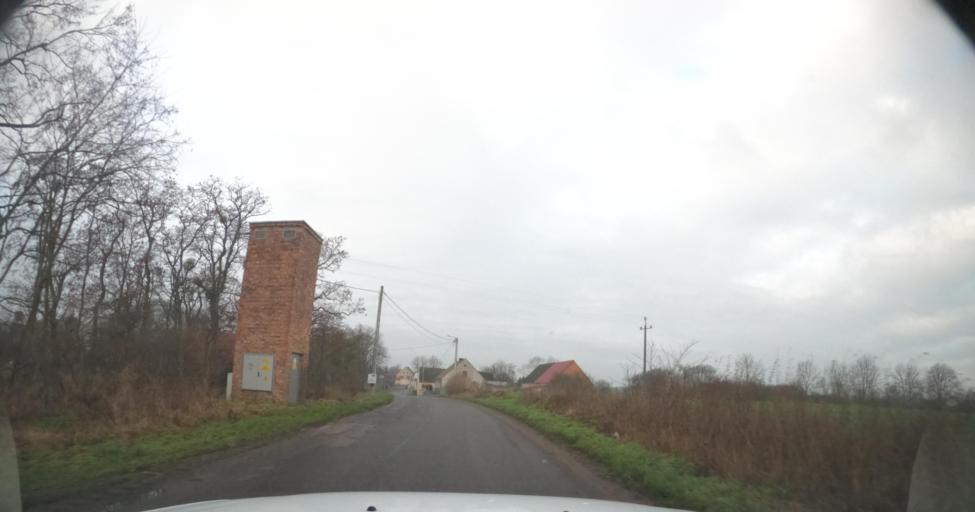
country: PL
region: West Pomeranian Voivodeship
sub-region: Powiat mysliborski
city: Boleszkowice
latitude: 52.7405
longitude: 14.6155
